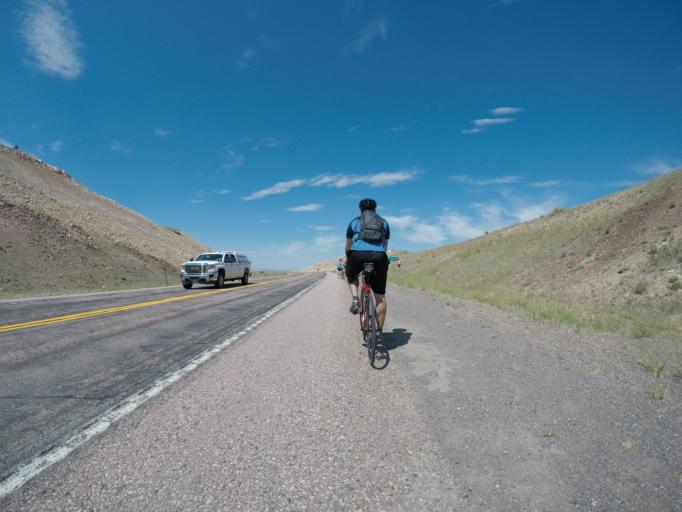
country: US
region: Wyoming
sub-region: Albany County
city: Laramie
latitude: 41.6866
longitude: -105.5186
